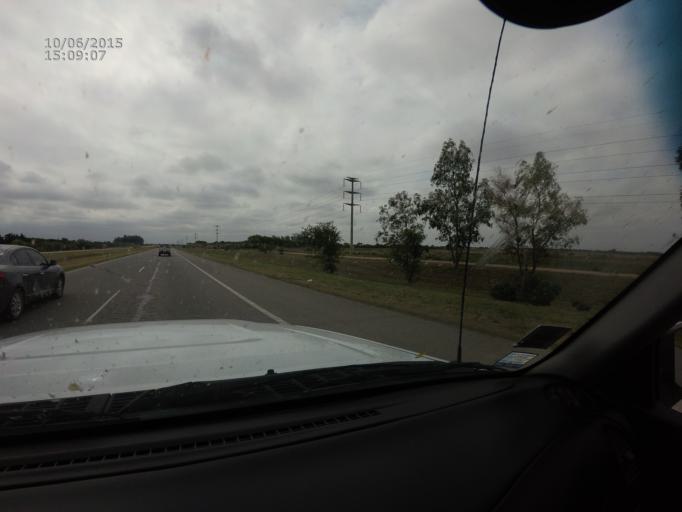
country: AR
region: Cordoba
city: Pilar
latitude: -31.6408
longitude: -63.8657
